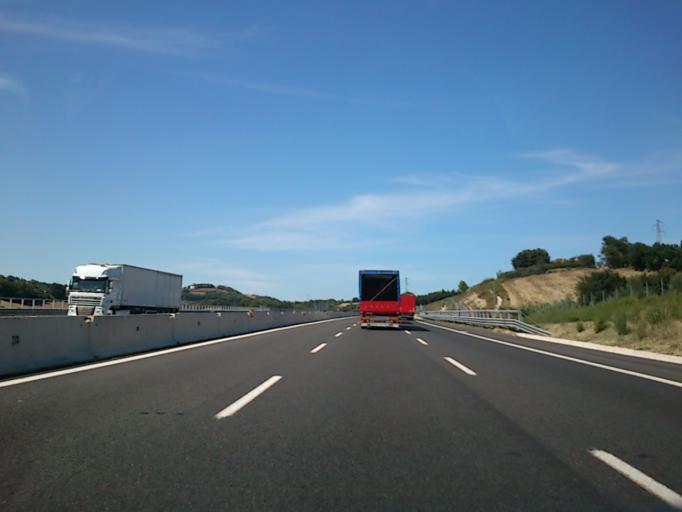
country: IT
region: The Marches
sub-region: Provincia di Pesaro e Urbino
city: Fenile
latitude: 43.8480
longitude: 12.9642
